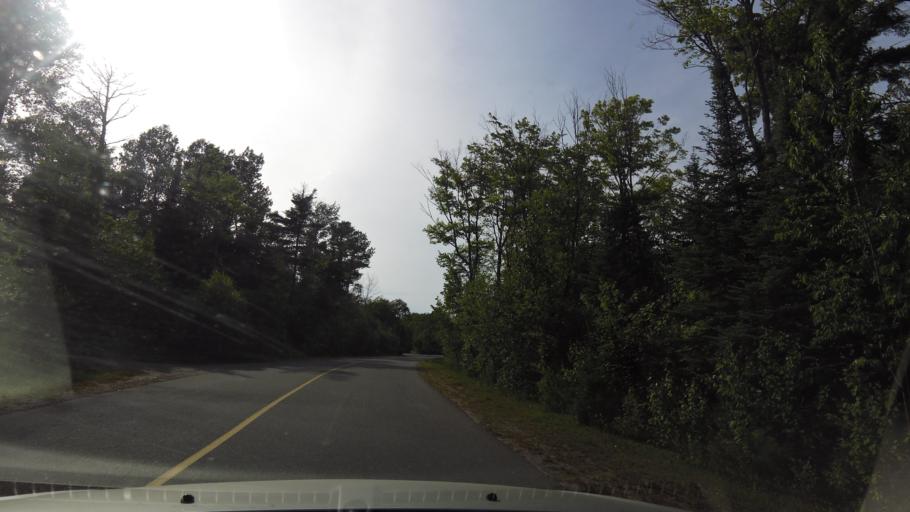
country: CA
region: Ontario
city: Greater Sudbury
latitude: 46.0149
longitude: -80.5831
